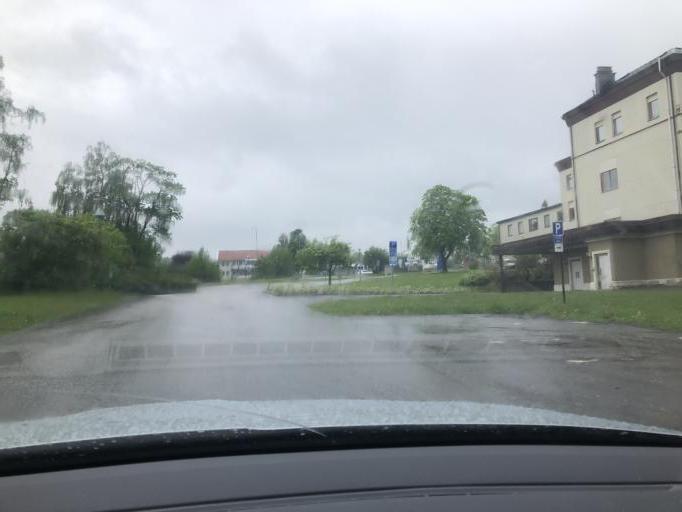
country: SE
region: Vaesternorrland
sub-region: Haernoesands Kommun
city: Haernoesand
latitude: 62.6241
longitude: 17.9285
